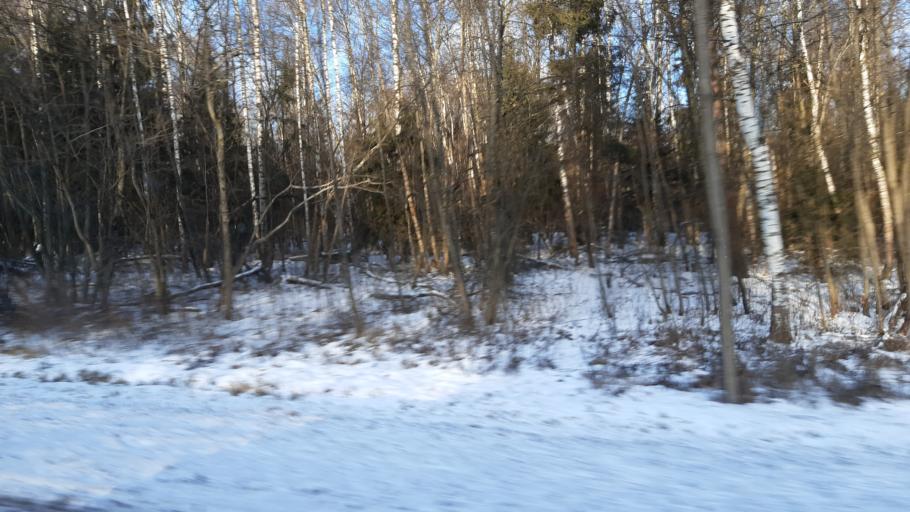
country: RU
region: Vladimir
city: Arsaki
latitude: 56.2917
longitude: 38.3793
